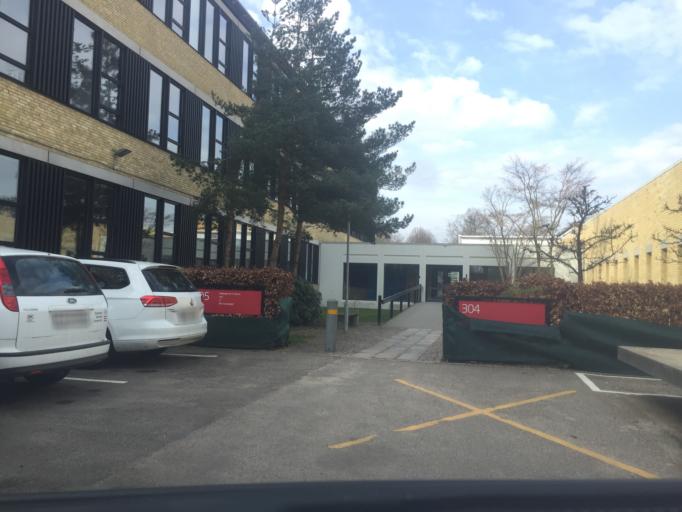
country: DK
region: Capital Region
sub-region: Lyngby-Tarbaek Kommune
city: Kongens Lyngby
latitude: 55.7841
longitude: 12.5200
